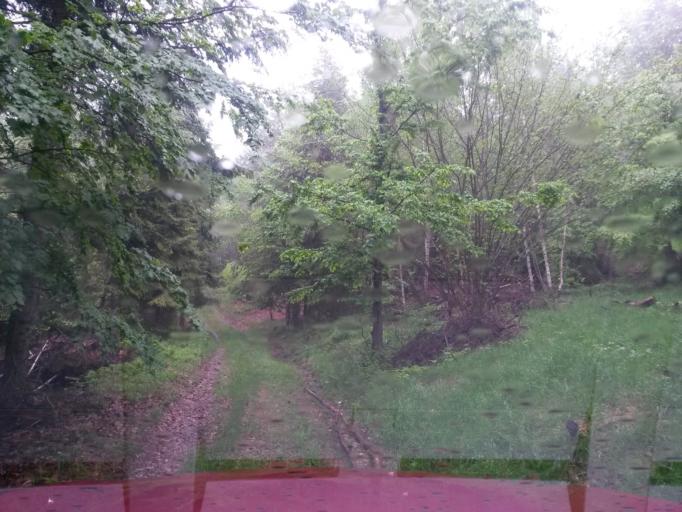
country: SK
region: Kosicky
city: Medzev
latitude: 48.7886
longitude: 20.7876
